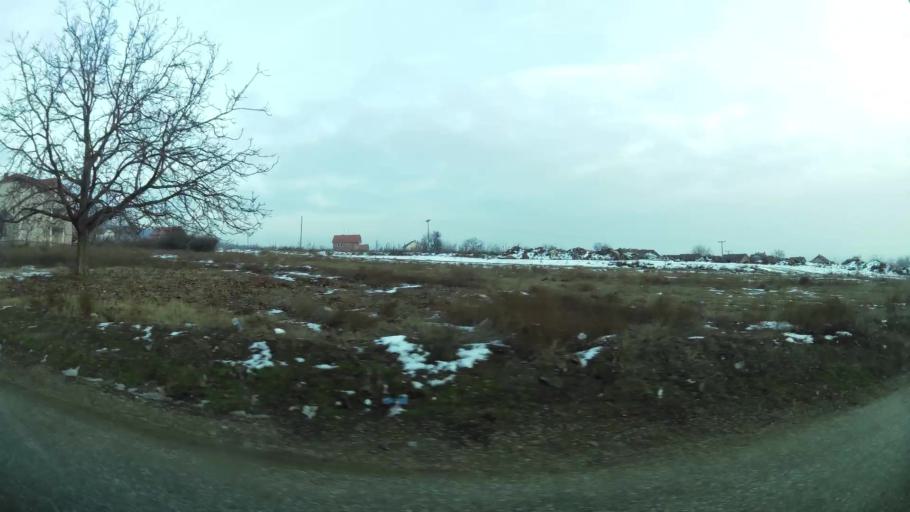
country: MK
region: Aracinovo
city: Arachinovo
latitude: 42.0296
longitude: 21.5458
